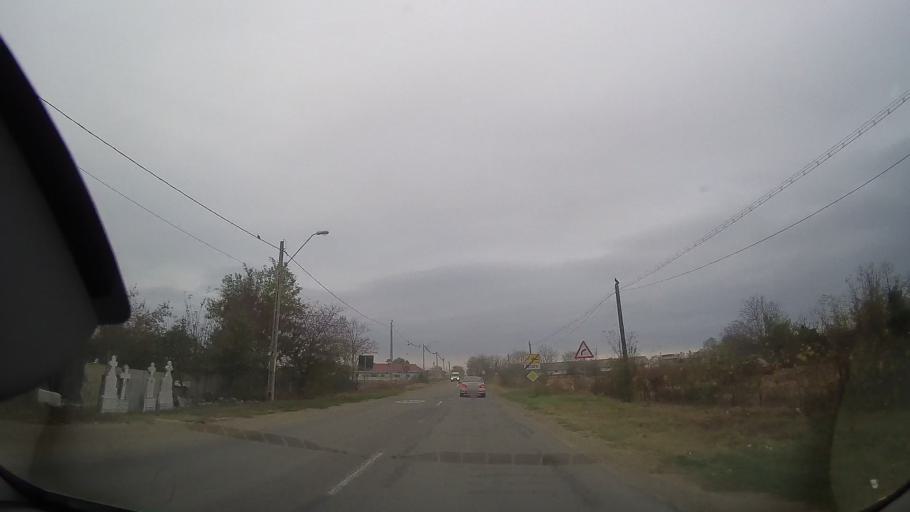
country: RO
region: Ialomita
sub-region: Oras Amara
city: Amara
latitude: 44.6211
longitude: 27.3043
